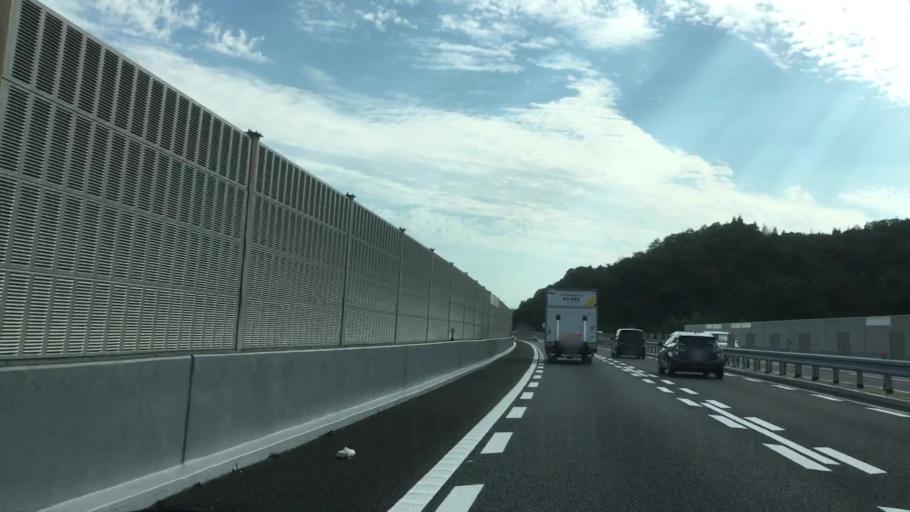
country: JP
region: Hiroshima
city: Ono-hara
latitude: 34.3142
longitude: 132.2809
